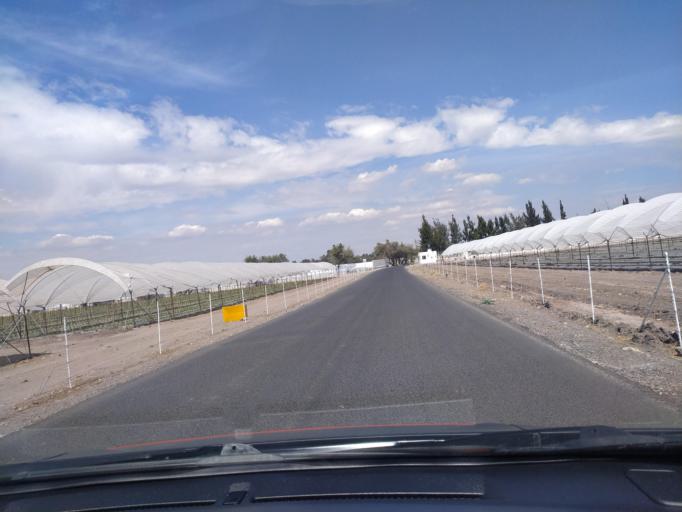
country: MX
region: Guanajuato
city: San Roque
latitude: 20.9621
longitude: -101.8300
